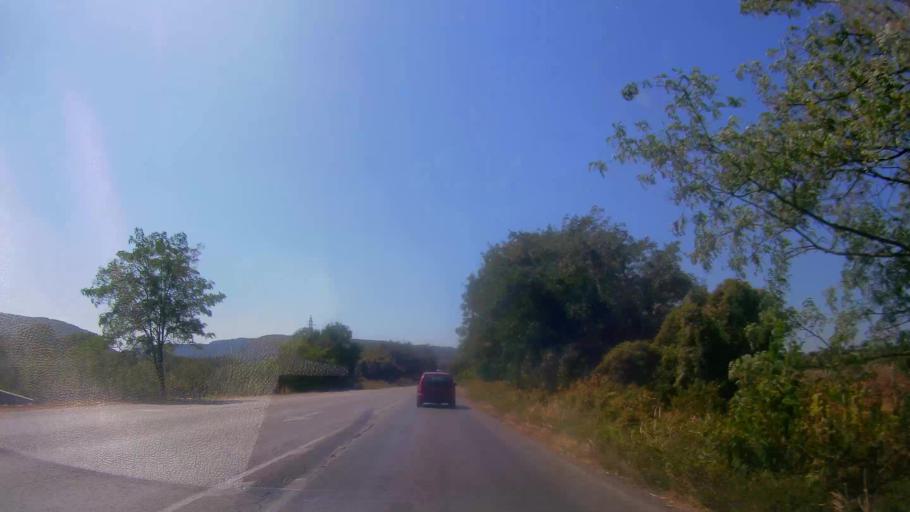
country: BG
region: Veliko Turnovo
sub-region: Obshtina Gorna Oryakhovitsa
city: Purvomaytsi
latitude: 43.1504
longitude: 25.6168
